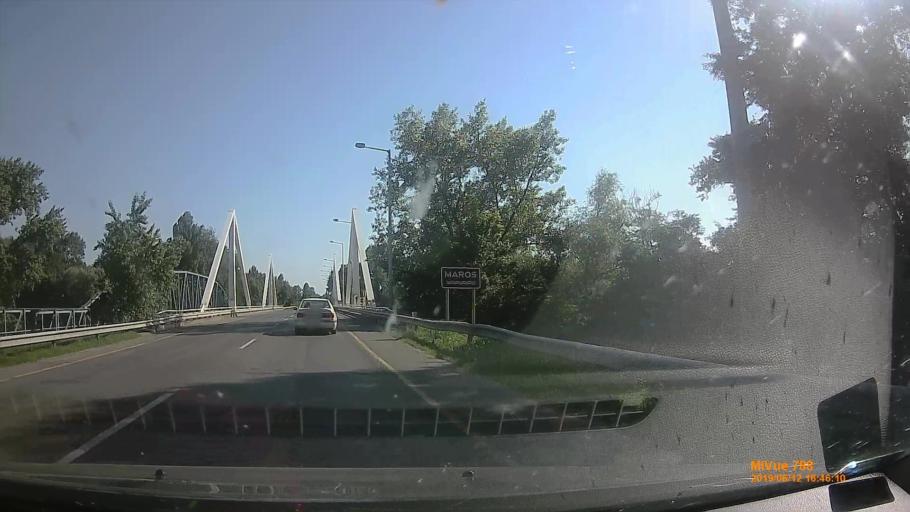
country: HU
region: Csongrad
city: Kiszombor
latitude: 46.2034
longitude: 20.4539
